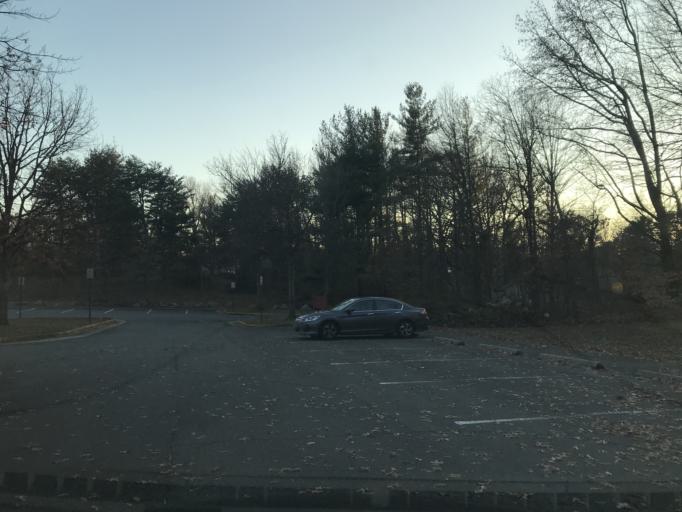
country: US
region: Virginia
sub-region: Fairfax County
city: Franconia
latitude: 38.7882
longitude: -77.1635
